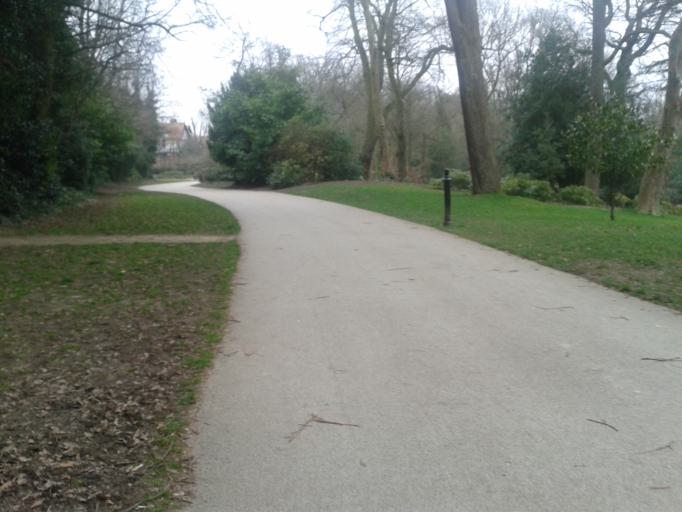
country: GB
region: England
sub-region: Greater London
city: Thornton Heath
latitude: 51.4245
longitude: -0.0686
